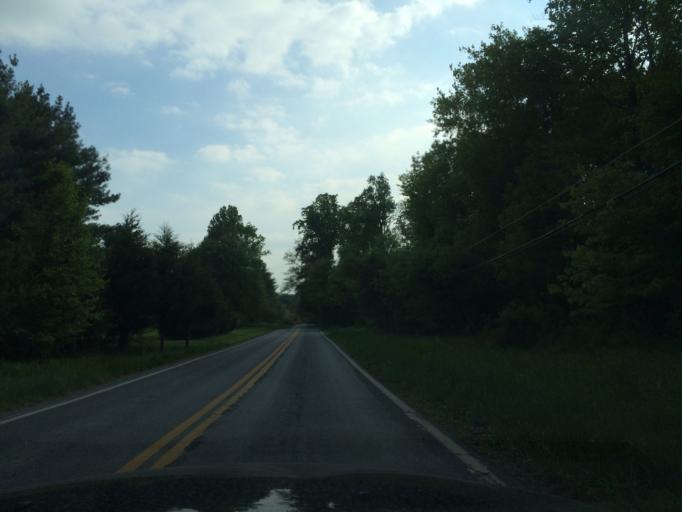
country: US
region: Maryland
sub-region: Howard County
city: Fulton
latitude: 39.1638
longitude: -76.9227
